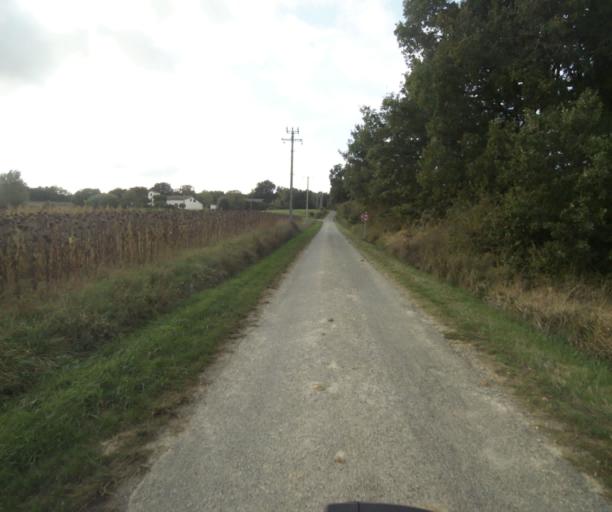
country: FR
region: Midi-Pyrenees
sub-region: Departement de la Haute-Garonne
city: Launac
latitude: 43.8087
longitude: 1.1122
